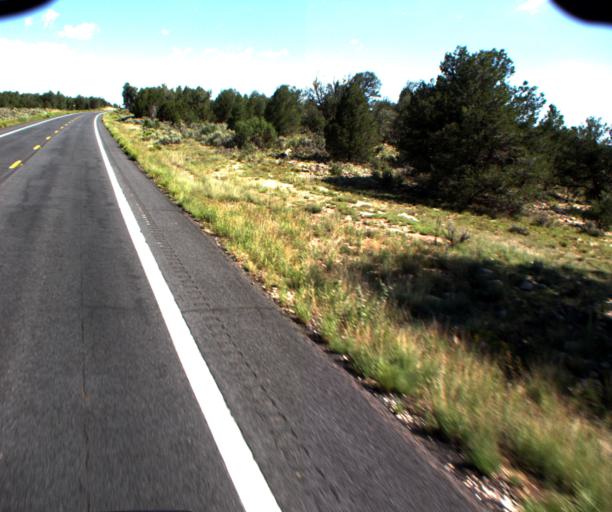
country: US
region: Arizona
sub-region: Coconino County
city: Grand Canyon Village
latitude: 35.8507
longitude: -112.1334
